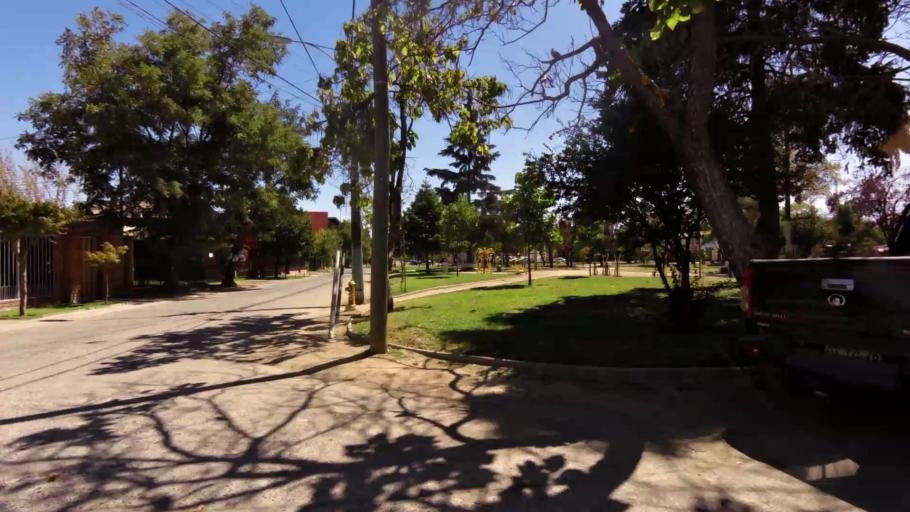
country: CL
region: O'Higgins
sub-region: Provincia de Cachapoal
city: Rancagua
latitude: -34.1685
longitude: -70.7306
